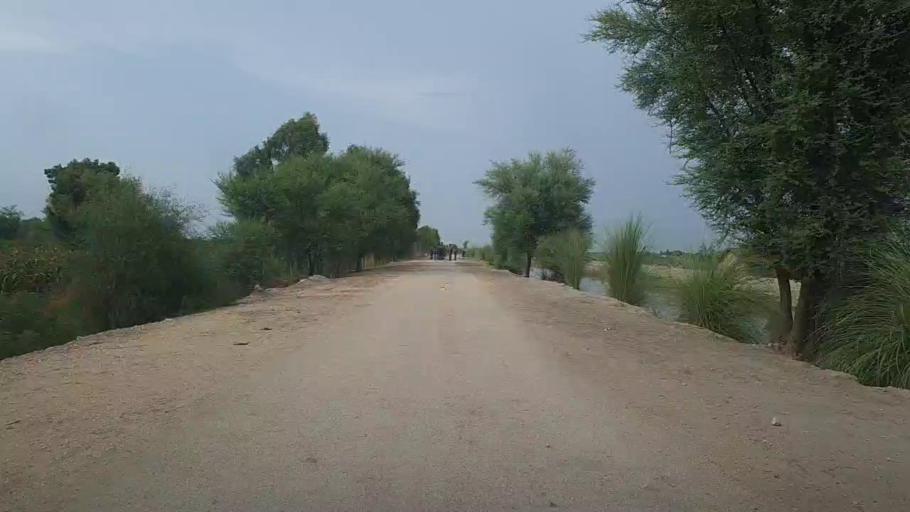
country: PK
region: Sindh
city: Karaundi
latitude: 26.9611
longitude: 68.4256
